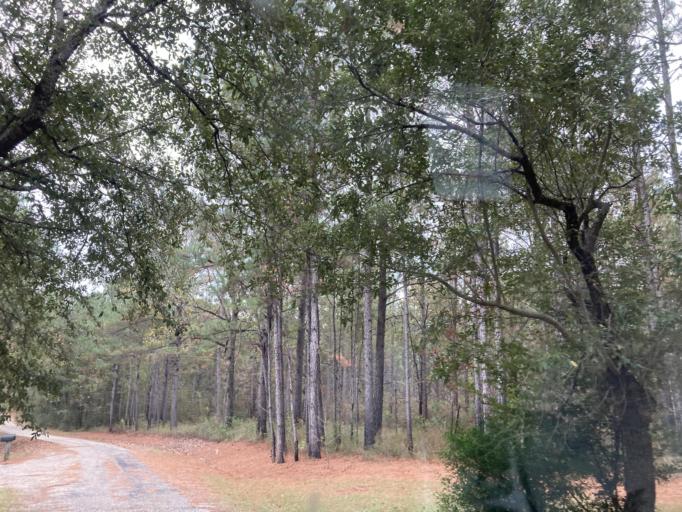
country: US
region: Mississippi
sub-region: Lamar County
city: Lumberton
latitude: 31.0541
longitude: -89.5149
